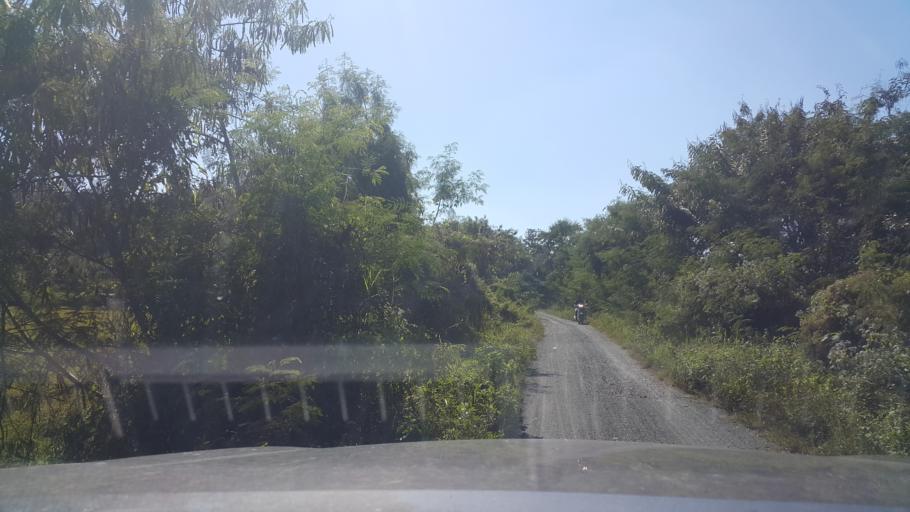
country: TH
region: Chiang Mai
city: Mae On
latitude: 18.7794
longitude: 99.2630
